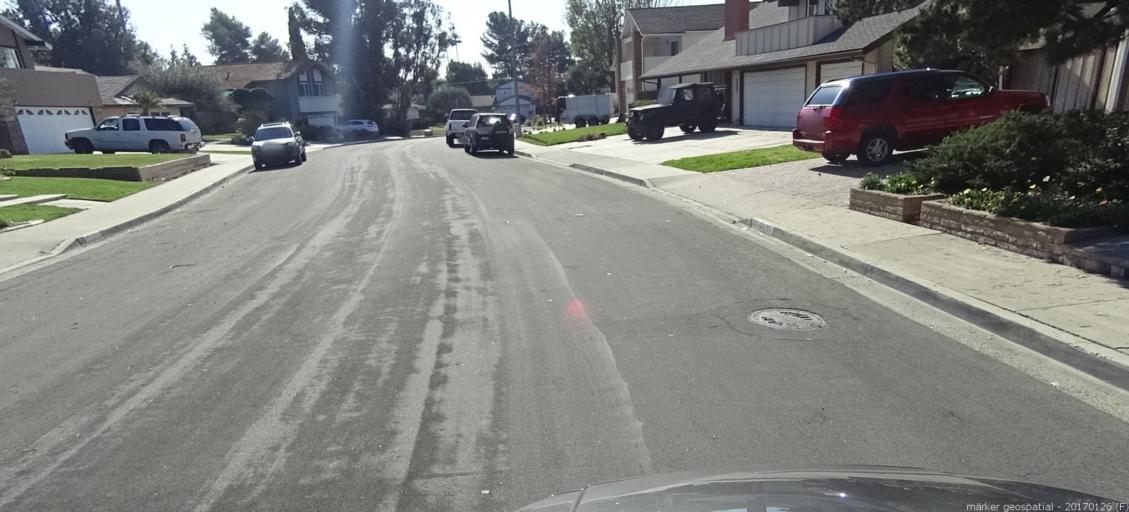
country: US
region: California
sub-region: Orange County
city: Lake Forest
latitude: 33.6315
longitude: -117.6918
